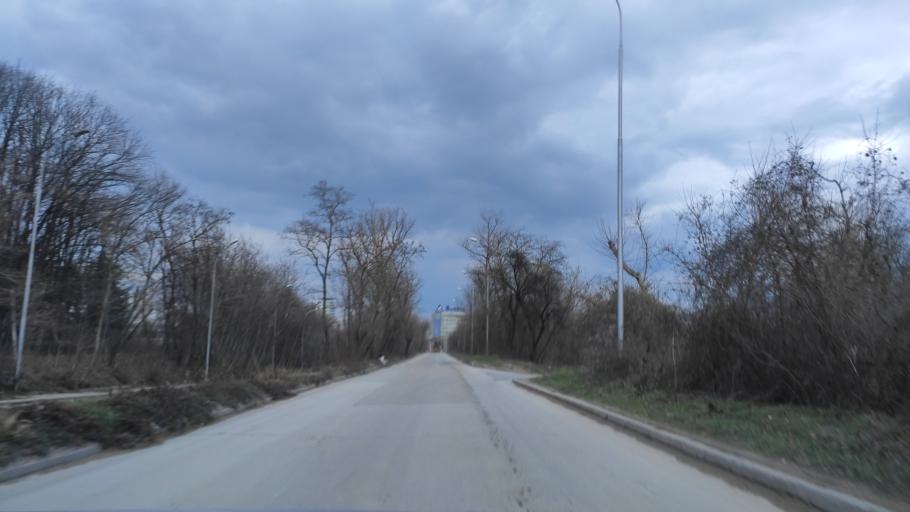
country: BG
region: Varna
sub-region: Obshtina Varna
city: Varna
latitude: 43.2240
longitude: 27.8647
